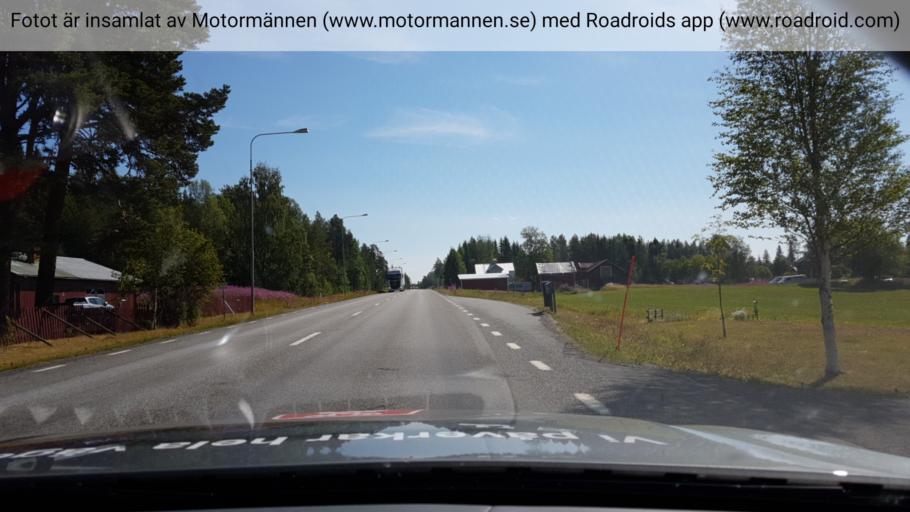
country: SE
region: Jaemtland
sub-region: OEstersunds Kommun
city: Lit
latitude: 63.3963
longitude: 15.0019
